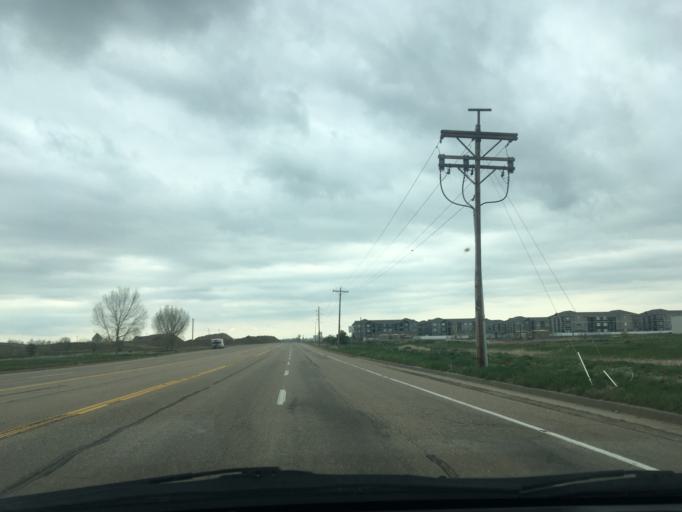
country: US
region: Colorado
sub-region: Weld County
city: Mead
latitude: 40.1679
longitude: -104.9781
